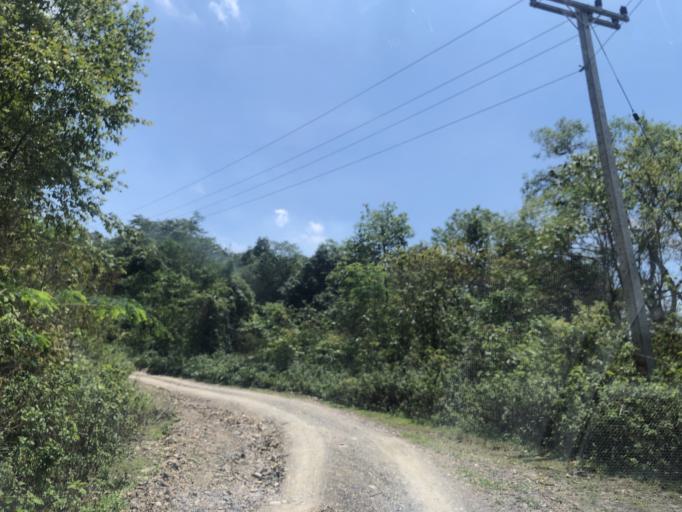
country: LA
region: Phongsali
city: Phongsali
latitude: 21.4416
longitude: 102.1631
